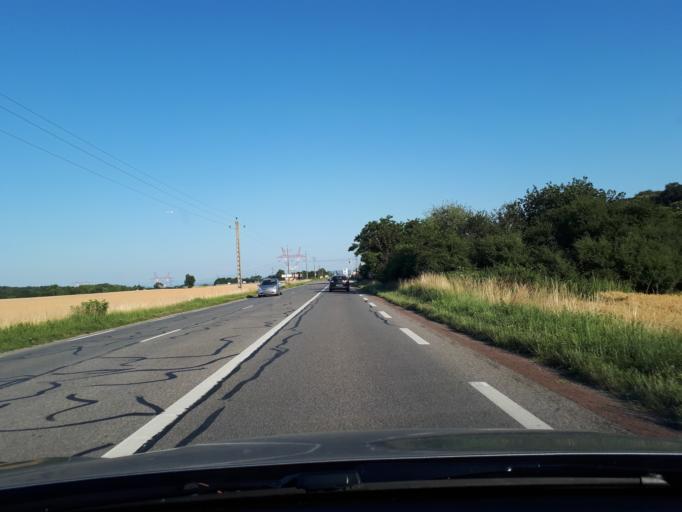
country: FR
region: Rhone-Alpes
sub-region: Departement de l'Isere
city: Grenay
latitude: 45.6756
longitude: 5.0763
